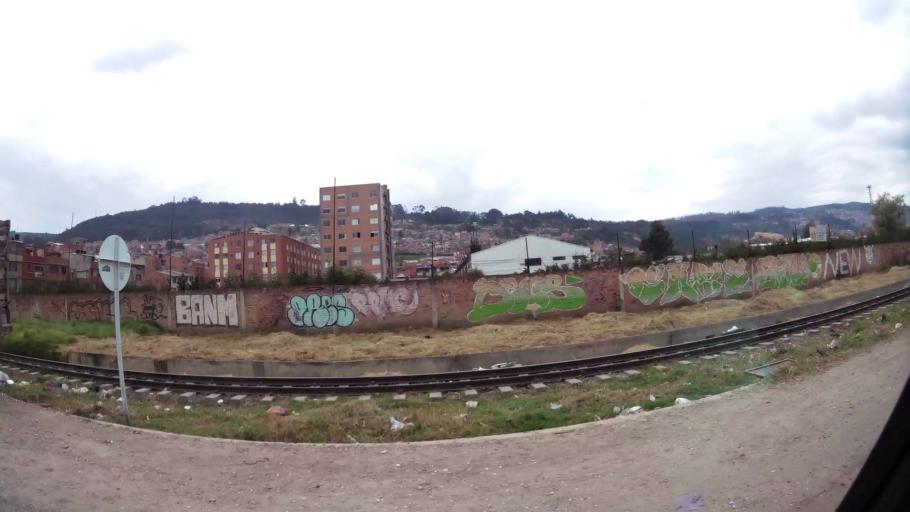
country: CO
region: Cundinamarca
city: La Calera
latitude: 4.7616
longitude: -74.0314
